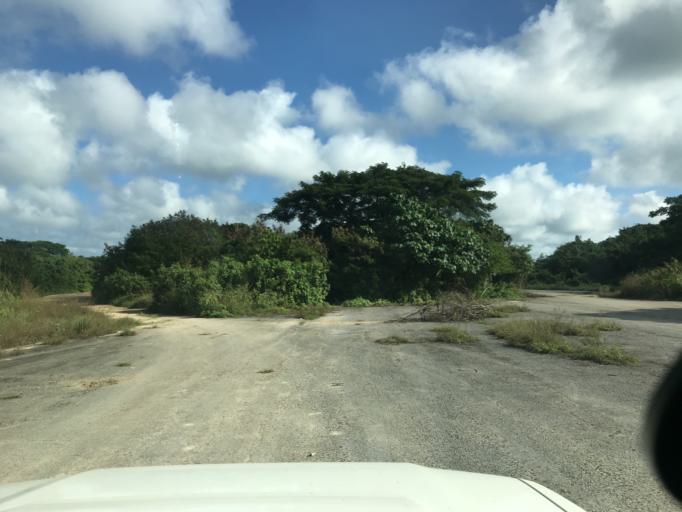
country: VU
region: Sanma
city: Luganville
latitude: -15.5104
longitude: 167.1258
